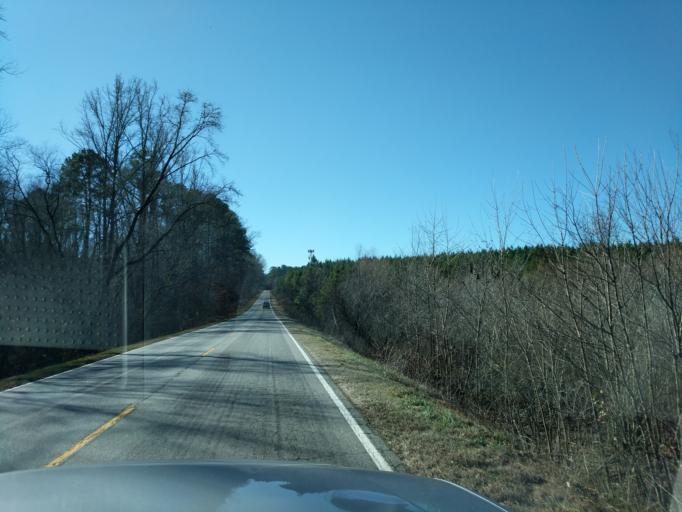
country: US
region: South Carolina
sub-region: Laurens County
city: Joanna
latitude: 34.2560
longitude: -81.8627
